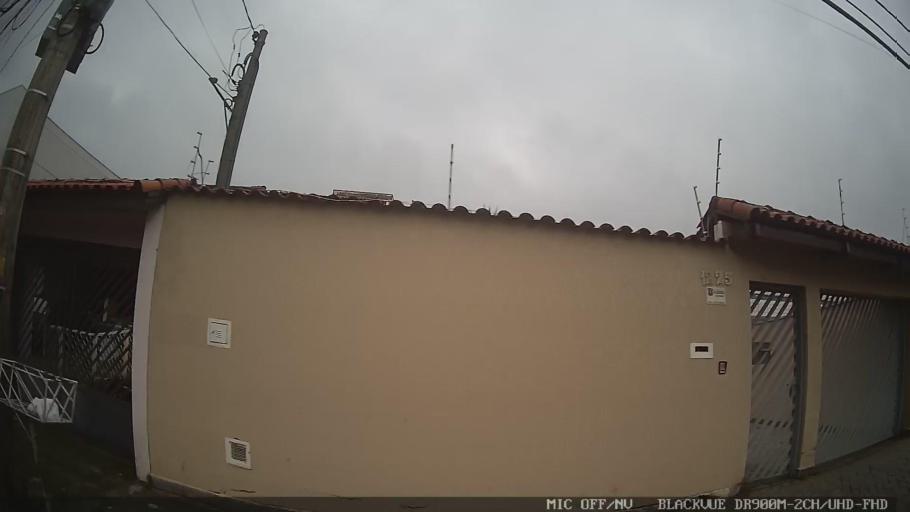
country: BR
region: Sao Paulo
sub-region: Mogi das Cruzes
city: Mogi das Cruzes
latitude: -23.5226
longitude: -46.1675
